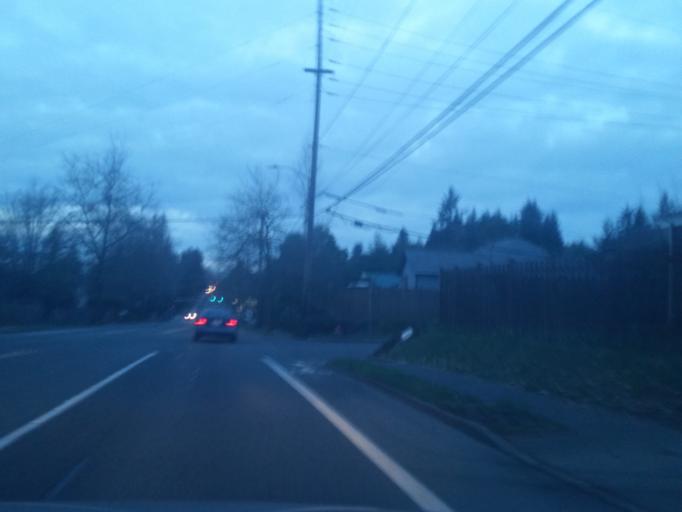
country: US
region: Washington
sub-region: King County
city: Shoreline
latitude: 47.7500
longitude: -122.3132
